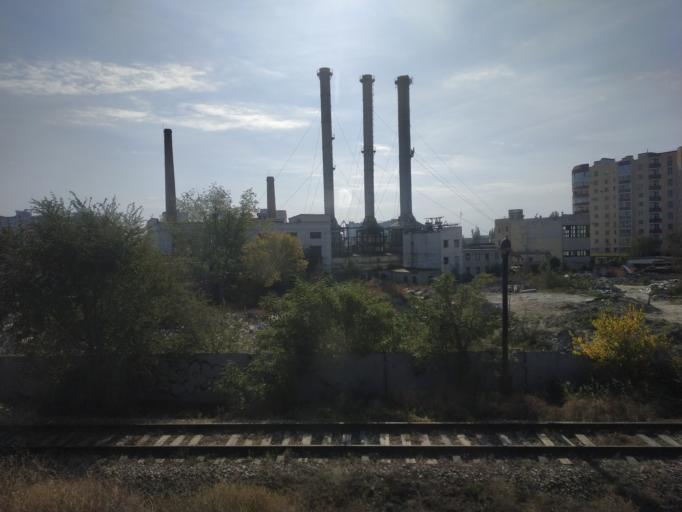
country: RU
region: Volgograd
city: Volgograd
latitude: 48.7326
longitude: 44.5348
